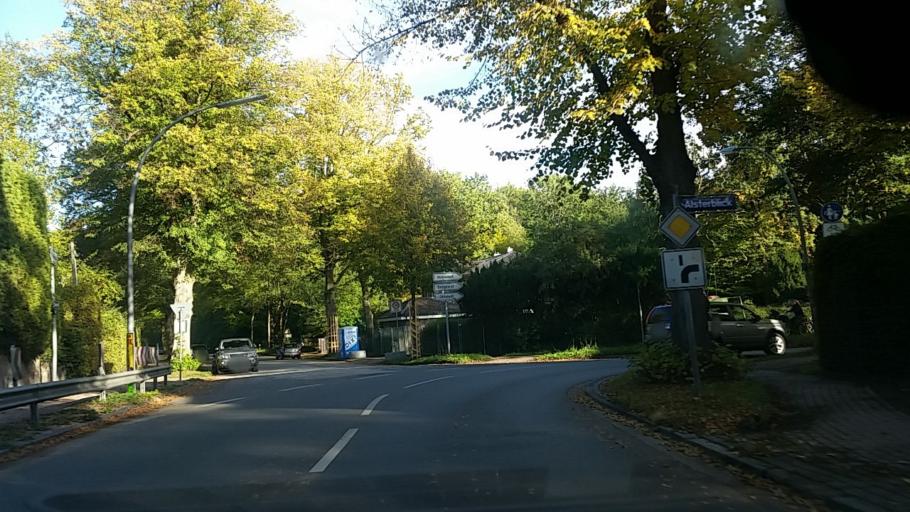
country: DE
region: Hamburg
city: Duvenstedt
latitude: 53.7047
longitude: 10.1197
